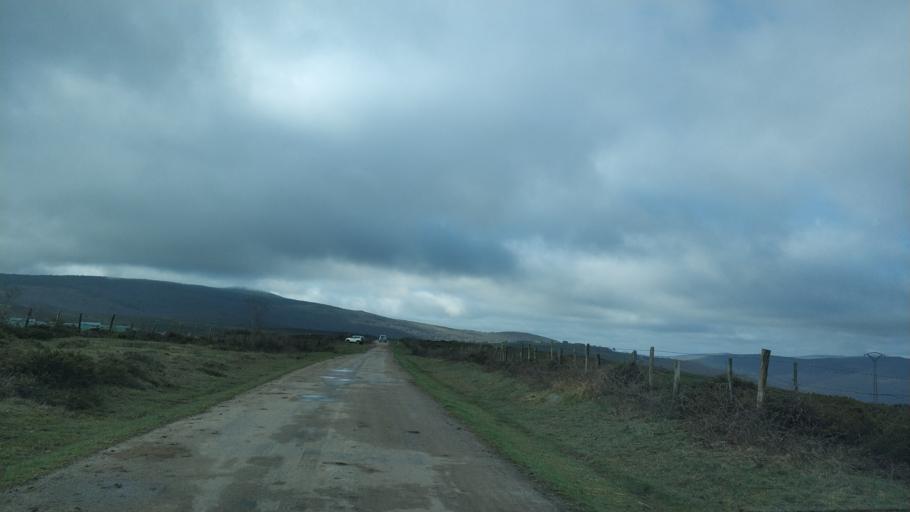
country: ES
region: Castille and Leon
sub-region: Provincia de Burgos
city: Arija
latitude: 42.9210
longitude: -3.9929
